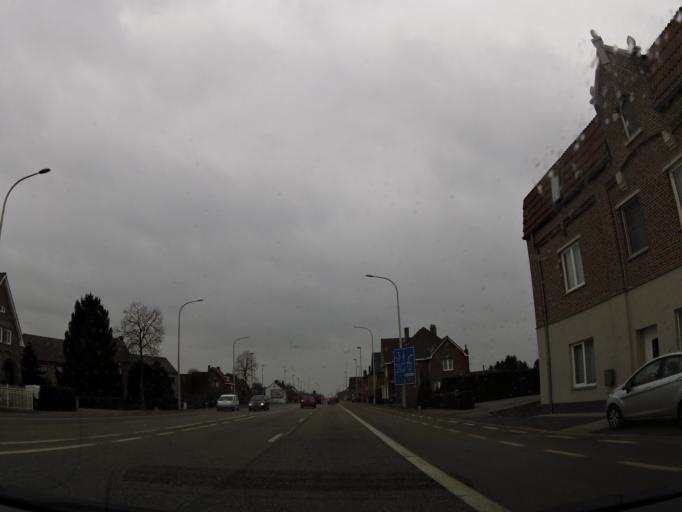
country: NL
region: Limburg
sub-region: Gemeente Stein
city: Berg
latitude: 51.0285
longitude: 5.7273
